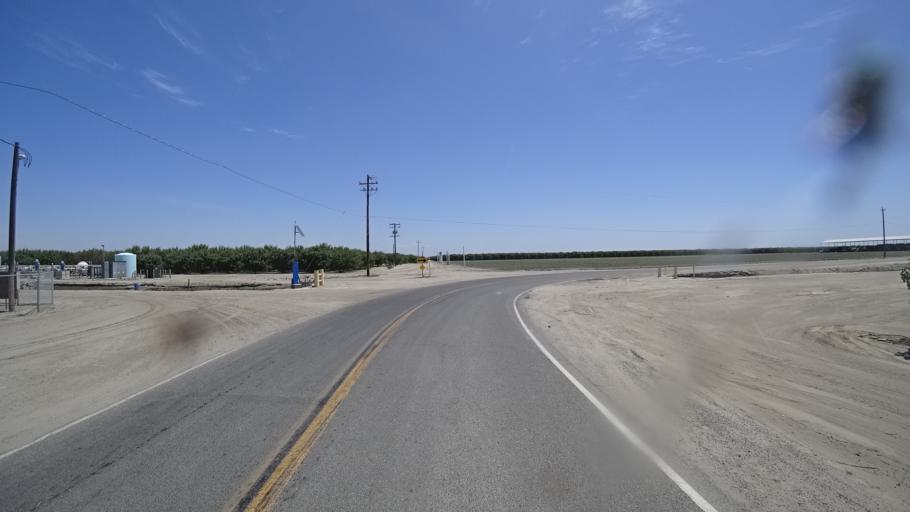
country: US
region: California
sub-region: Kings County
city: Corcoran
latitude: 36.1162
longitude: -119.6263
